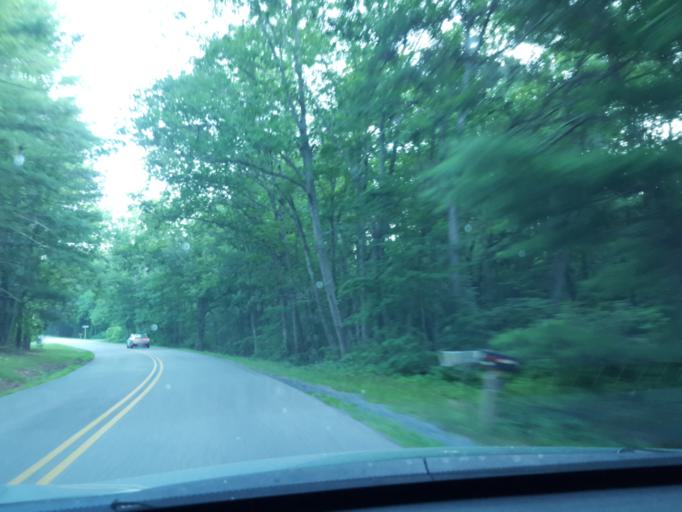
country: US
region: Virginia
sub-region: Augusta County
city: Lyndhurst
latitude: 37.9314
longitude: -78.9783
